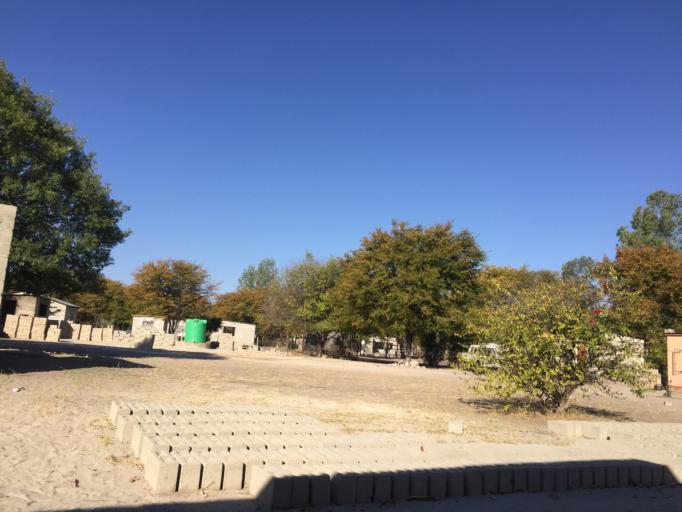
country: BW
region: North West
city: Maun
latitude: -19.9522
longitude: 23.4551
